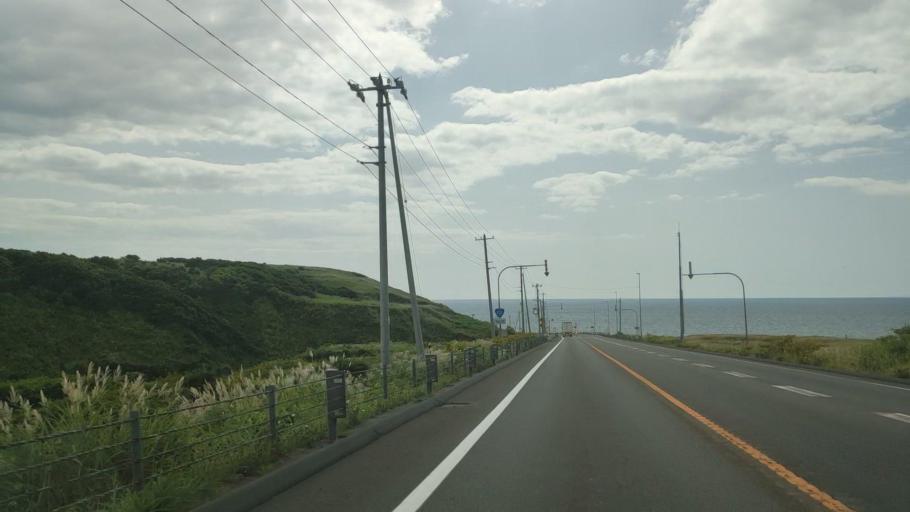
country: JP
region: Hokkaido
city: Rumoi
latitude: 44.5482
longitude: 141.7693
